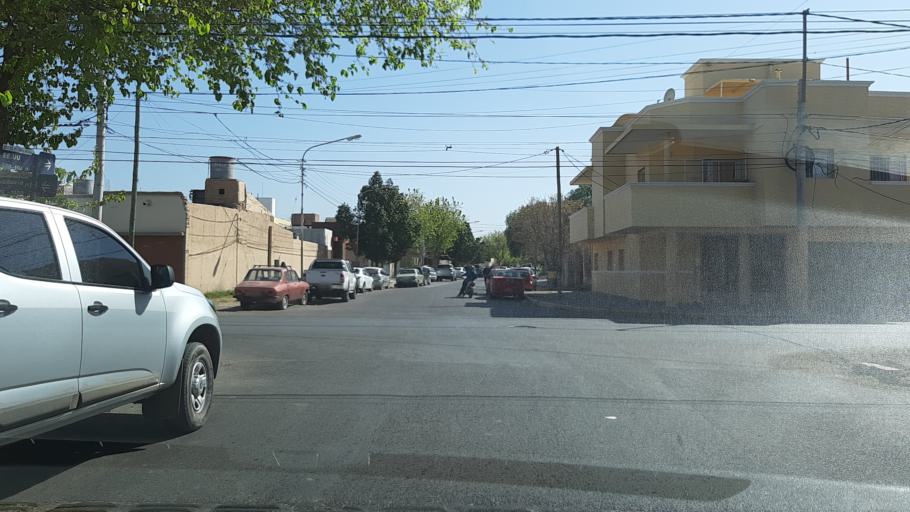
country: AR
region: San Juan
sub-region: Departamento de Santa Lucia
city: Santa Lucia
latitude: -31.5358
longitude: -68.5118
